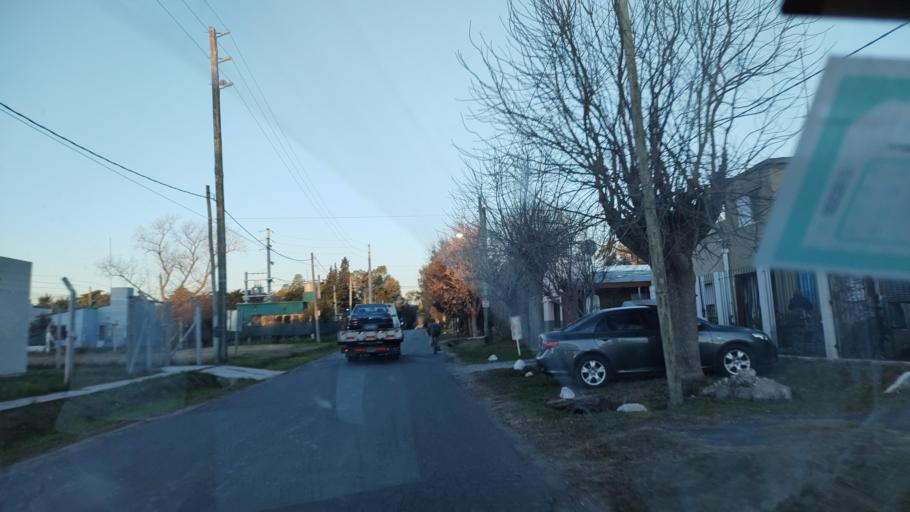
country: AR
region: Buenos Aires
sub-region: Partido de La Plata
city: La Plata
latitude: -34.9049
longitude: -58.0414
